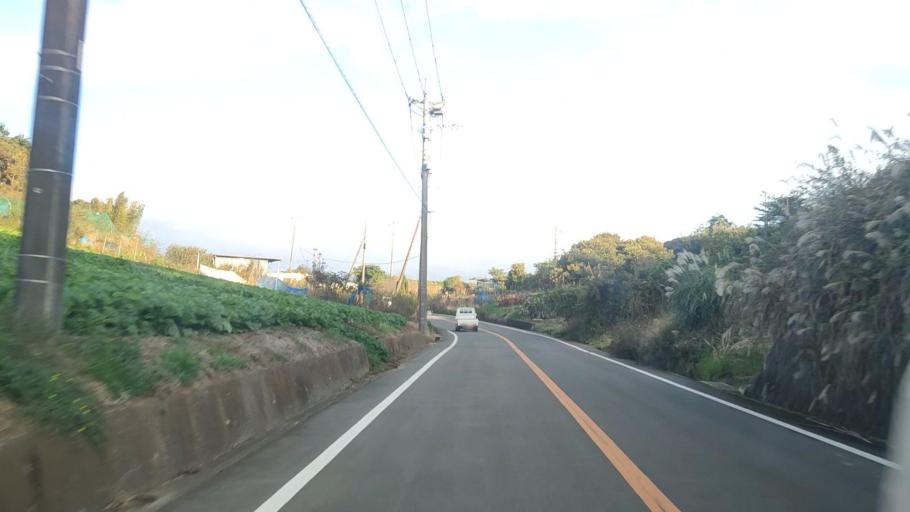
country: JP
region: Shizuoka
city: Mishima
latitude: 35.1337
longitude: 138.9638
